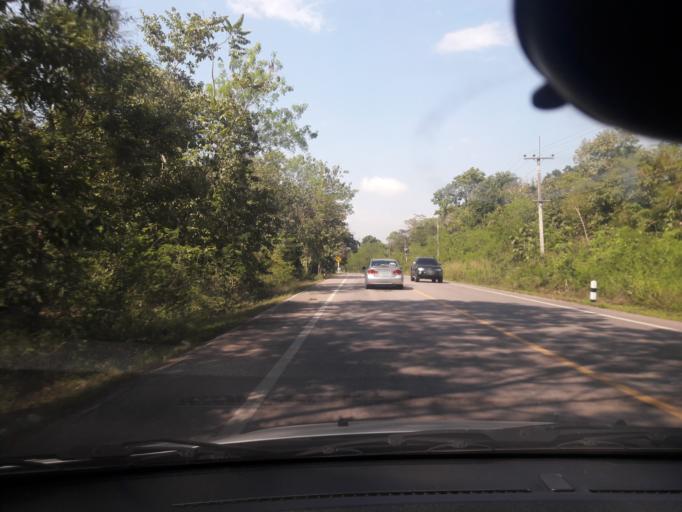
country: TH
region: Lampang
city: Mae Tha
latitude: 18.1878
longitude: 99.5386
